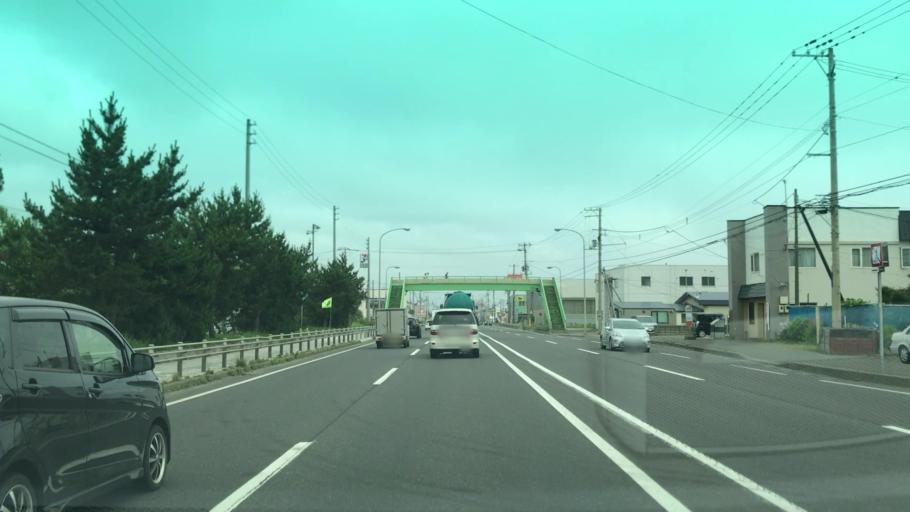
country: JP
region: Hokkaido
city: Muroran
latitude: 42.3612
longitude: 141.0545
